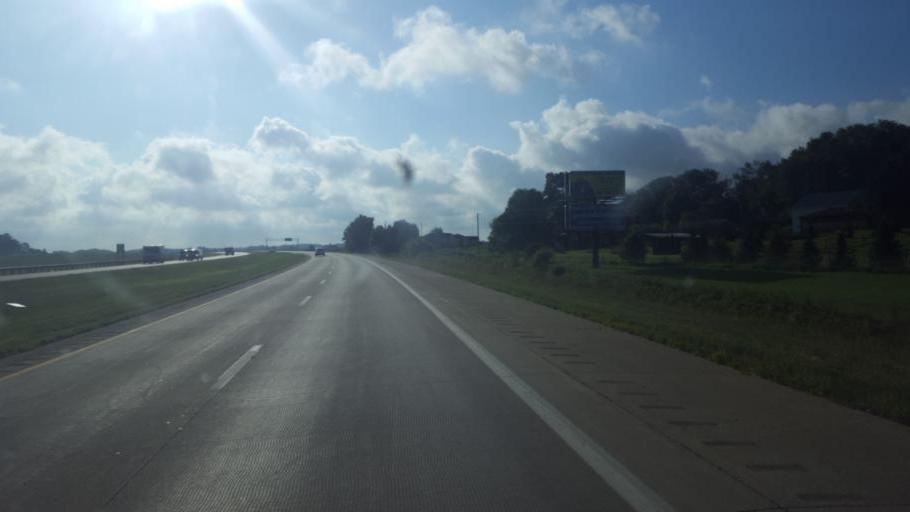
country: US
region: Ohio
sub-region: Wayne County
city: Apple Creek
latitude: 40.7916
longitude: -81.8032
